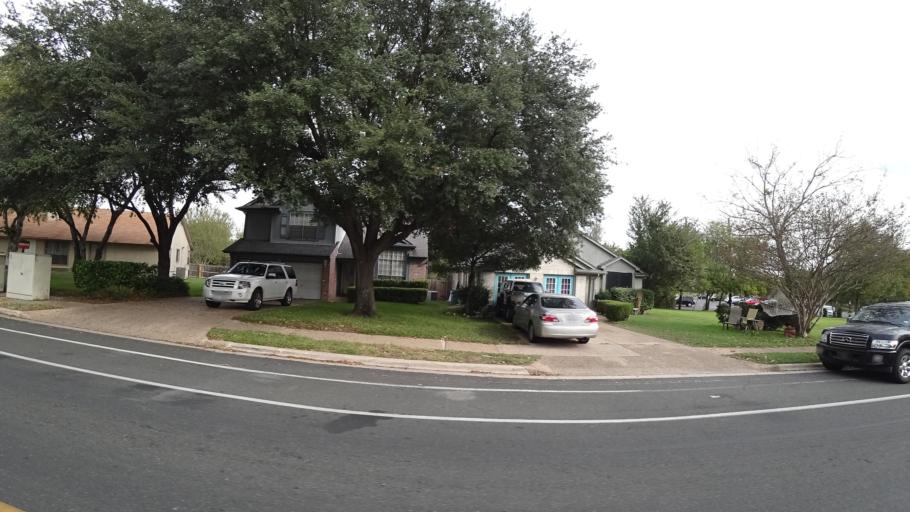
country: US
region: Texas
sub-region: Travis County
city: Wells Branch
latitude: 30.4467
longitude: -97.6761
